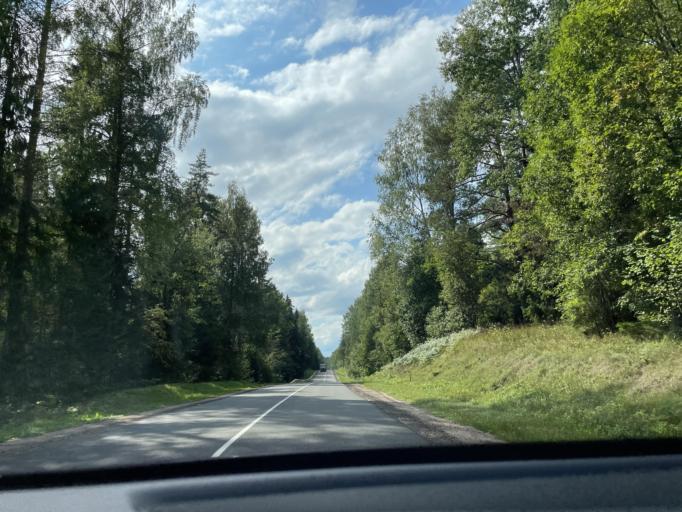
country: RU
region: Novgorod
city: Valday
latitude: 58.0318
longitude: 33.2121
